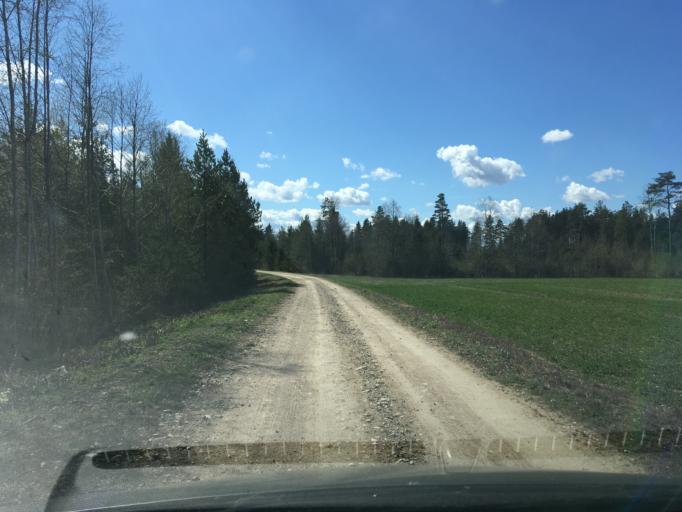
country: EE
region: Harju
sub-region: Raasiku vald
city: Raasiku
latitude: 59.2189
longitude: 25.1465
